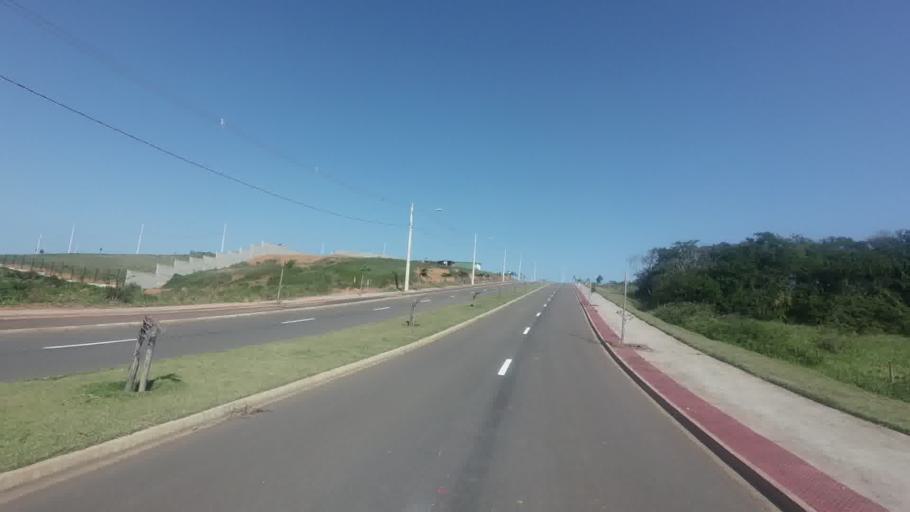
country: BR
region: Espirito Santo
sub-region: Guarapari
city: Guarapari
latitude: -20.7121
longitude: -40.5358
